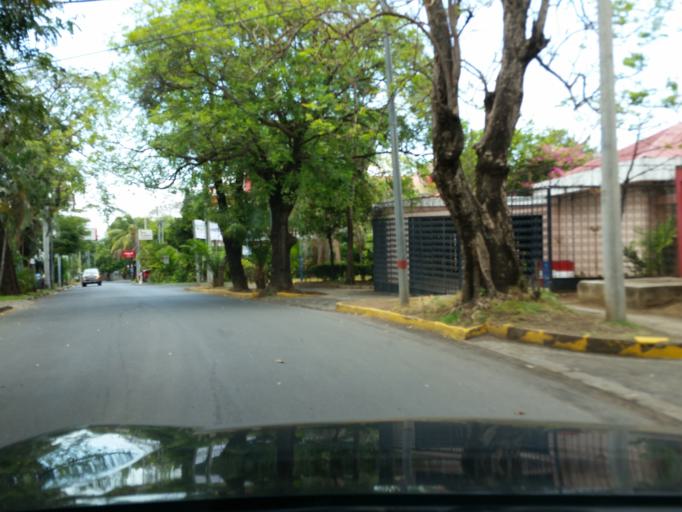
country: NI
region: Managua
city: Managua
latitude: 12.1176
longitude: -86.2625
